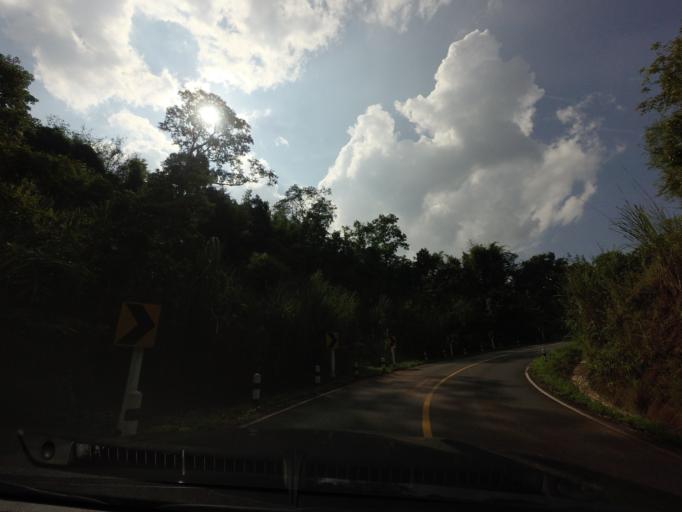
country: TH
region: Uttaradit
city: Ban Khok
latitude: 18.1983
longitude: 101.0526
